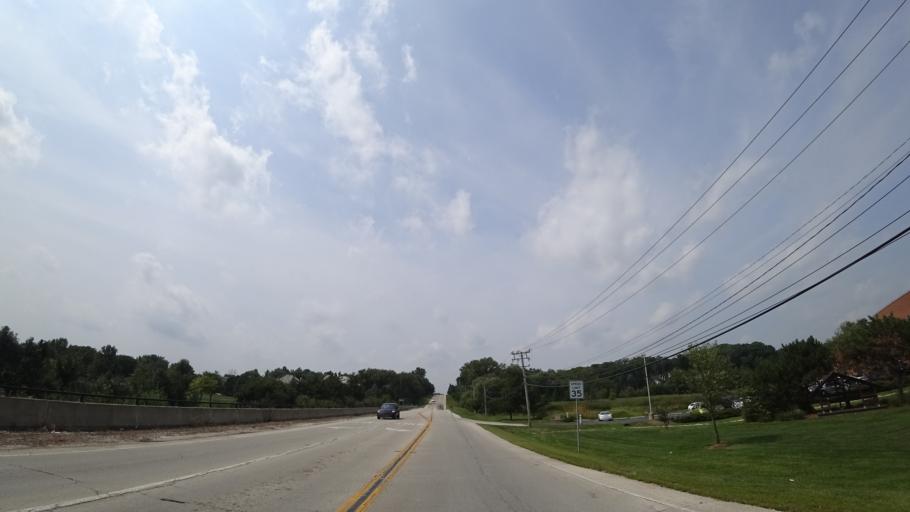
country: US
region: Illinois
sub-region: Cook County
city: Orland Park
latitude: 41.6153
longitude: -87.8921
